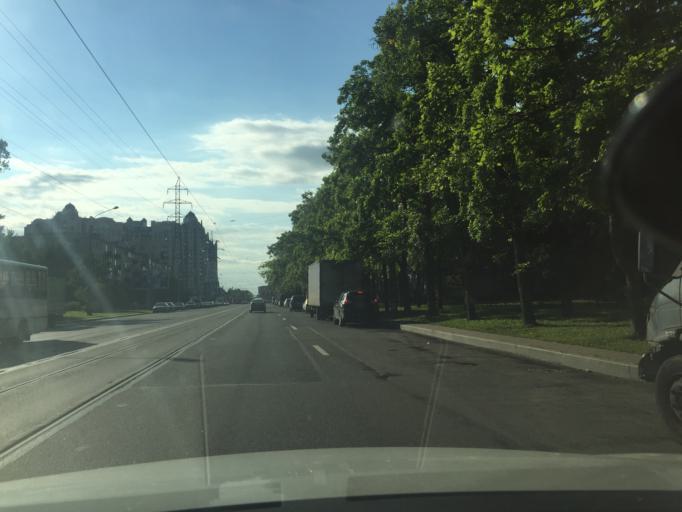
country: RU
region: St.-Petersburg
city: Kupchino
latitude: 59.8354
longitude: 30.3443
